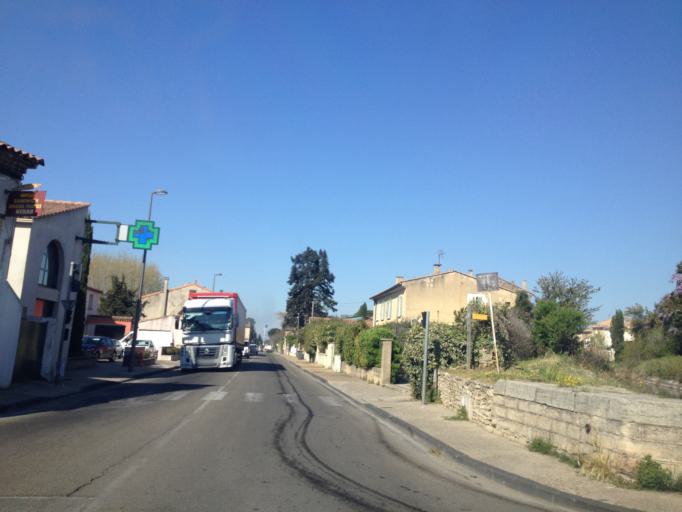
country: FR
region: Provence-Alpes-Cote d'Azur
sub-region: Departement du Vaucluse
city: Carpentras
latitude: 44.0608
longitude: 5.0487
